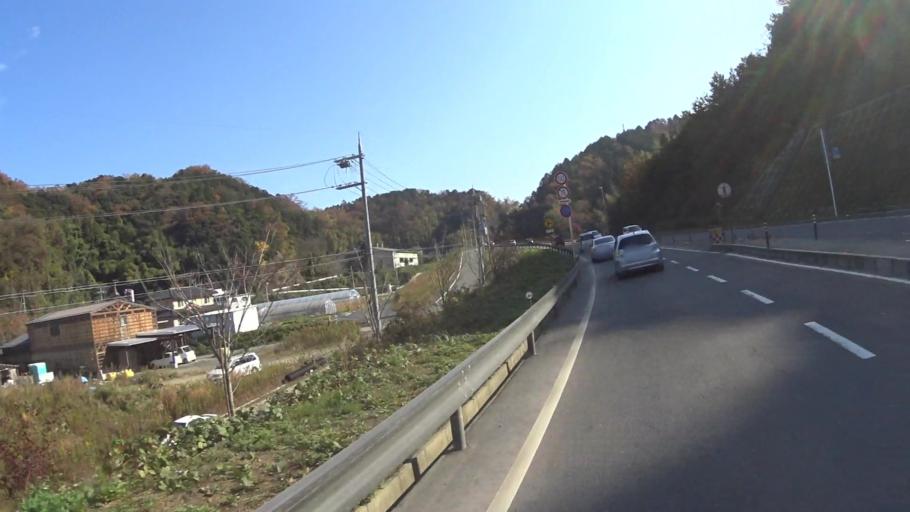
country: JP
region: Kyoto
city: Maizuru
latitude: 35.4502
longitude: 135.2701
